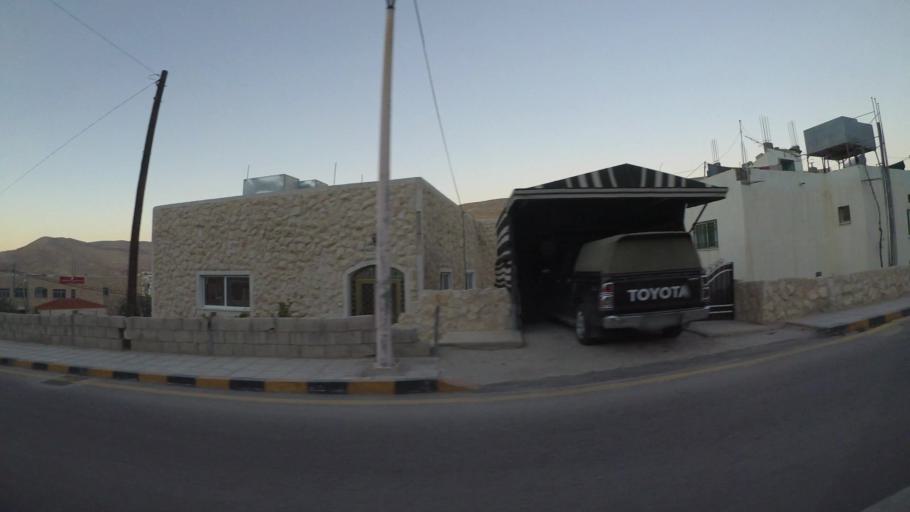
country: JO
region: Ma'an
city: Petra
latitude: 30.3122
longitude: 35.4787
